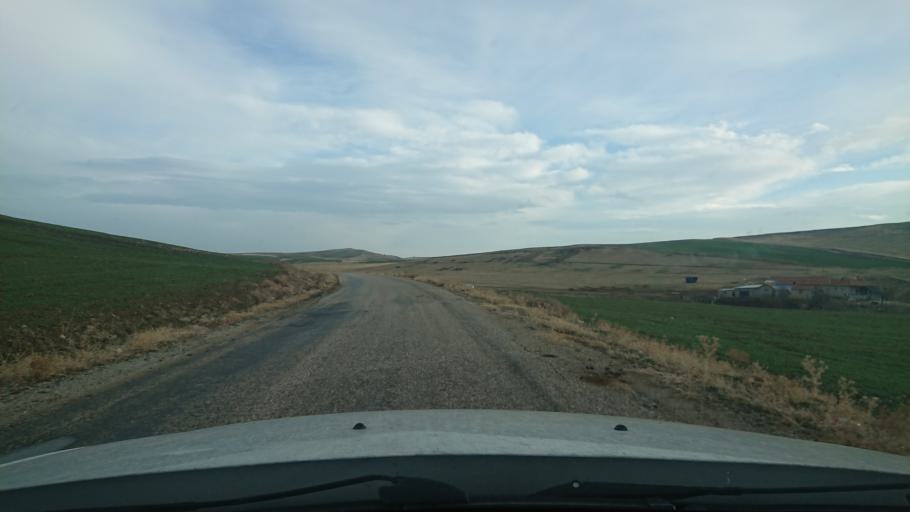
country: TR
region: Aksaray
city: Acipinar
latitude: 38.6382
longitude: 33.8059
